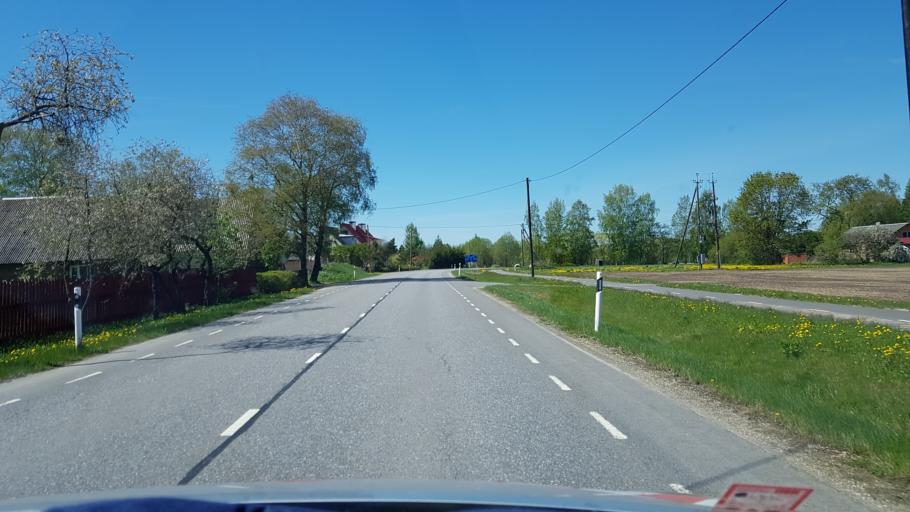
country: EE
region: Tartu
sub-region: Noo vald
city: Noo
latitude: 58.3176
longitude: 26.6247
